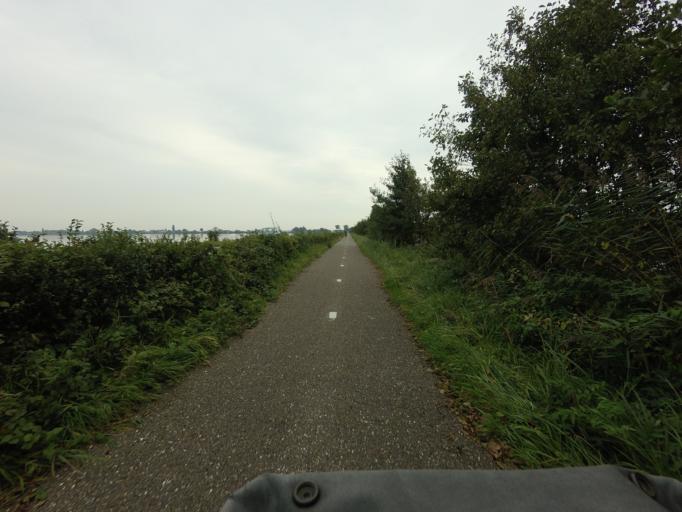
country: NL
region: North Holland
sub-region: Gemeente Wijdemeren
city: Oud-Loosdrecht
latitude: 52.2001
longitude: 5.0514
